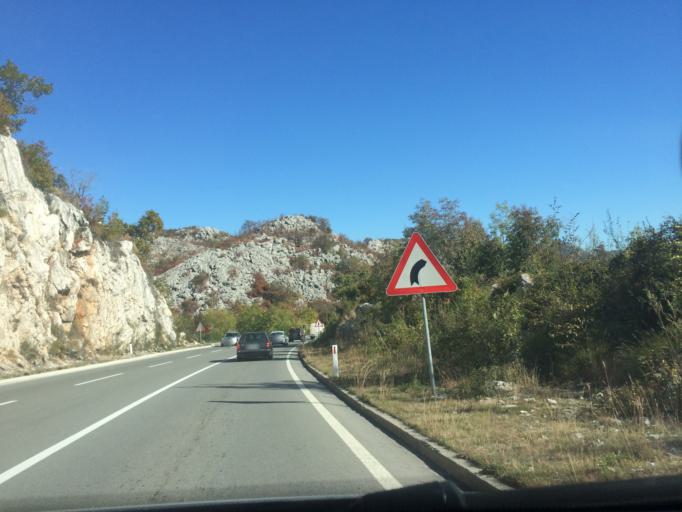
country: ME
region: Cetinje
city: Cetinje
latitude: 42.3773
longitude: 18.9806
